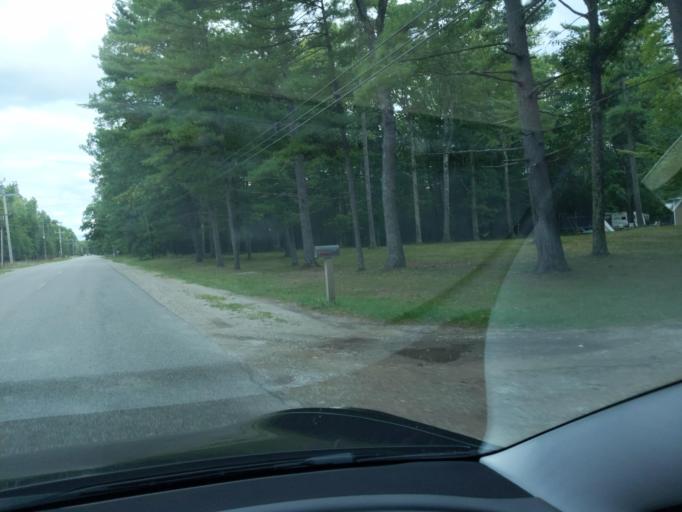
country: US
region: Michigan
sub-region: Kalkaska County
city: Rapid City
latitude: 44.8507
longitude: -85.3143
